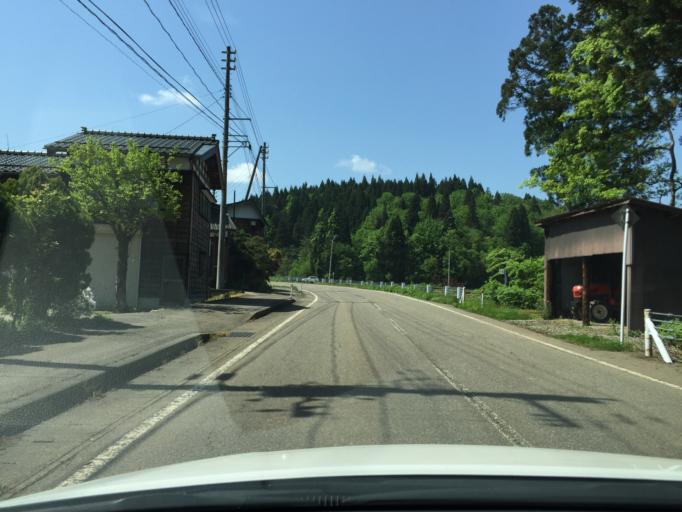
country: JP
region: Niigata
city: Tochio-honcho
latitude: 37.5404
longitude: 139.0922
